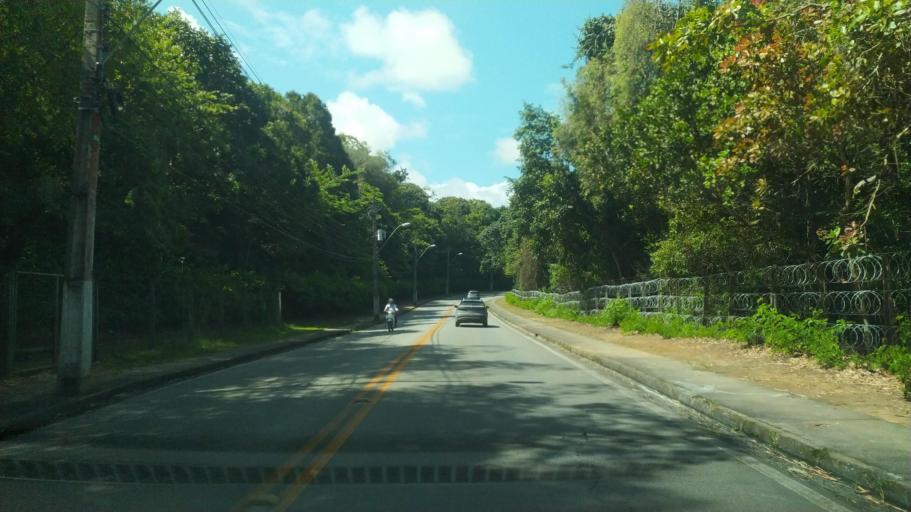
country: BR
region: Alagoas
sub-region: Maceio
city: Maceio
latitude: -9.5996
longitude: -35.7400
